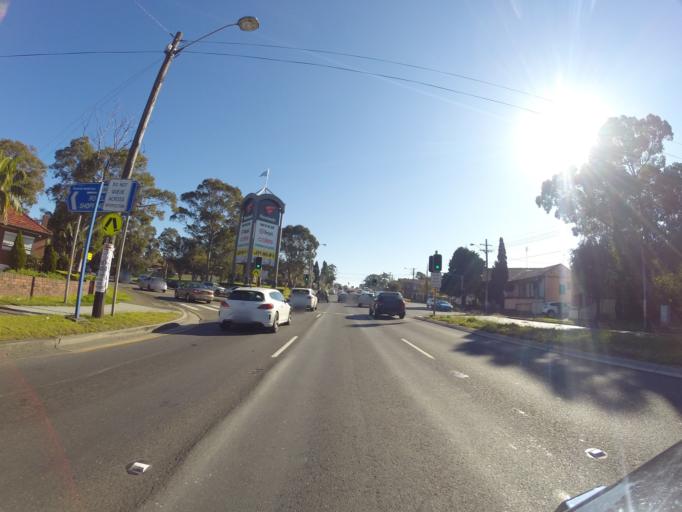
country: AU
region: New South Wales
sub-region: Canterbury
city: Roselands
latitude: -33.9373
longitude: 151.0745
